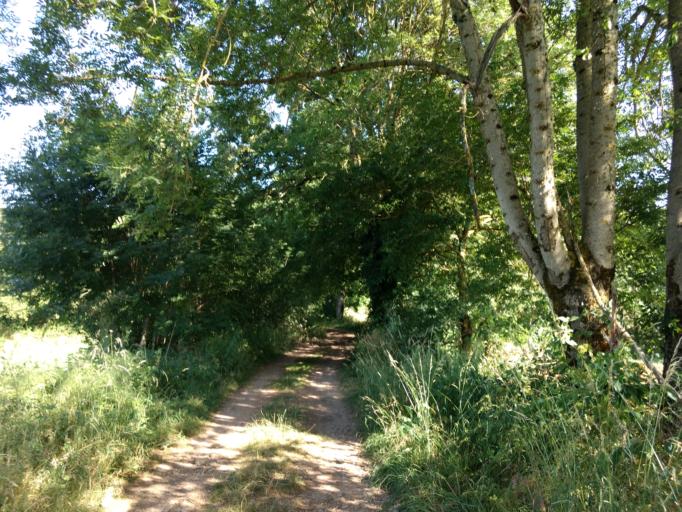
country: FR
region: Midi-Pyrenees
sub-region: Departement de l'Aveyron
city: La Loubiere
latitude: 44.3605
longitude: 2.6906
